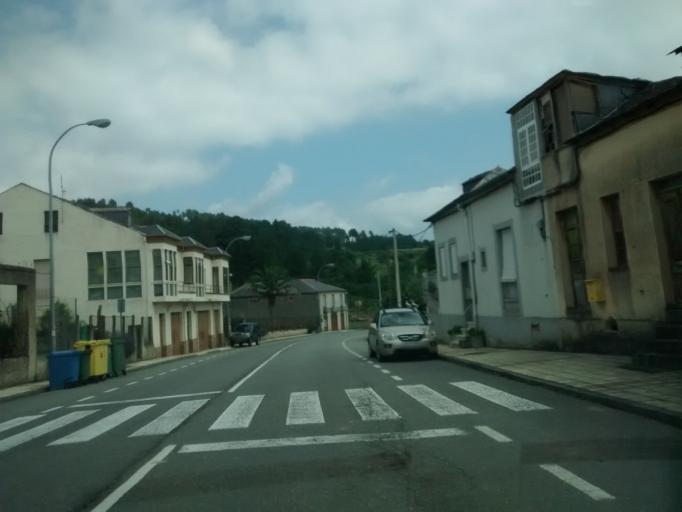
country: ES
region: Galicia
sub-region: Provincia de Ourense
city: Petin
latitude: 42.3456
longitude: -7.1701
